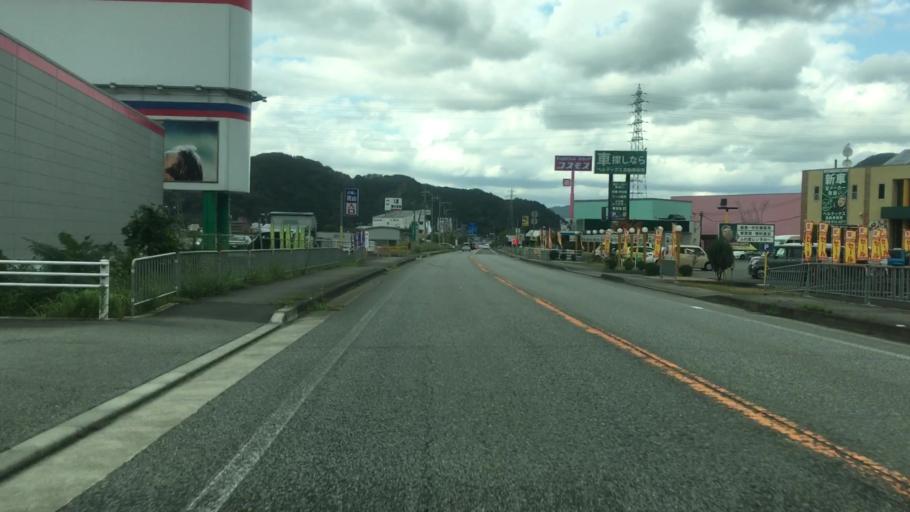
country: JP
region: Hyogo
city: Toyooka
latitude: 35.3290
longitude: 134.8682
